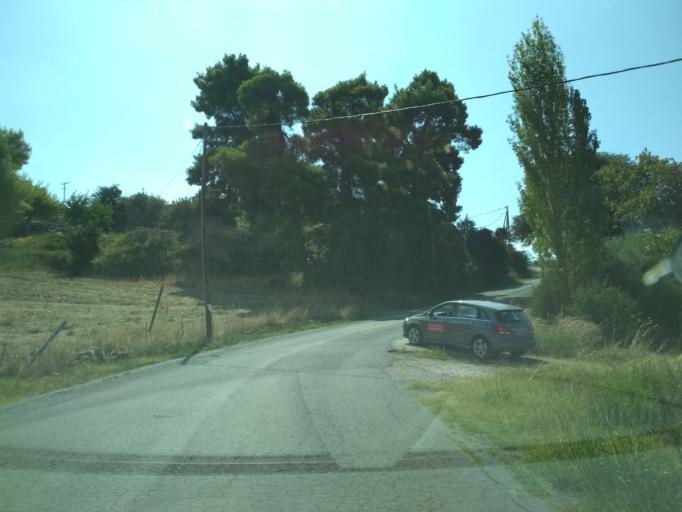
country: GR
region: Central Greece
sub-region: Nomos Evvoias
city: Roviai
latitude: 38.8196
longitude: 23.2683
